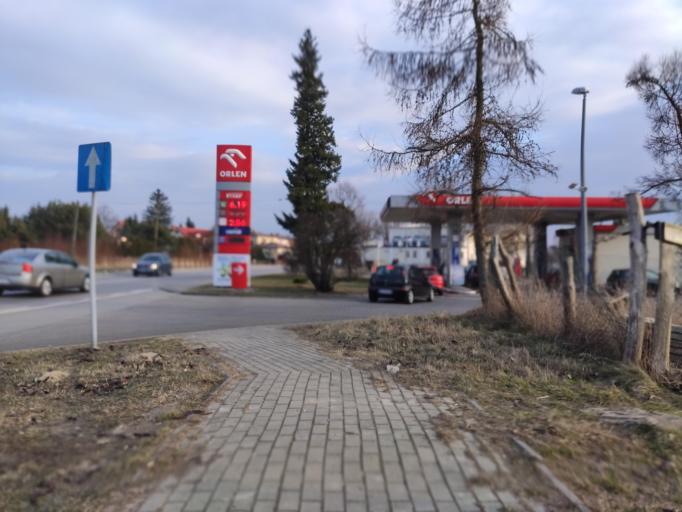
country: PL
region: Lublin Voivodeship
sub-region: Powiat lubartowski
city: Kock
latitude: 51.6438
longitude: 22.4458
